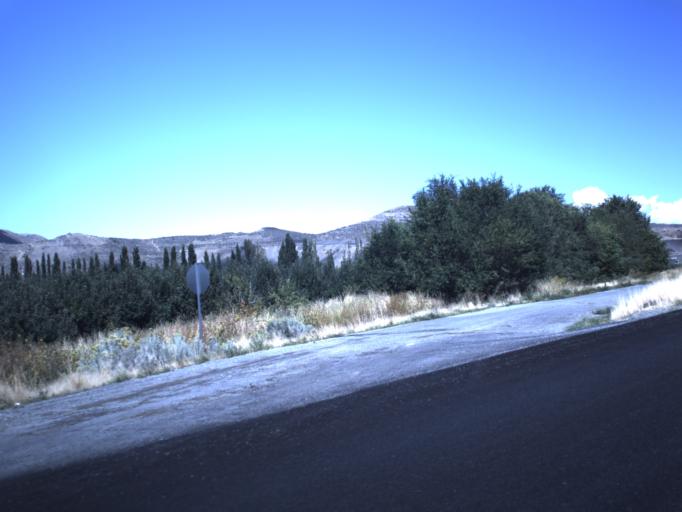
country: US
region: Utah
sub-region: Utah County
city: Genola
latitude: 40.0016
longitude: -111.8202
